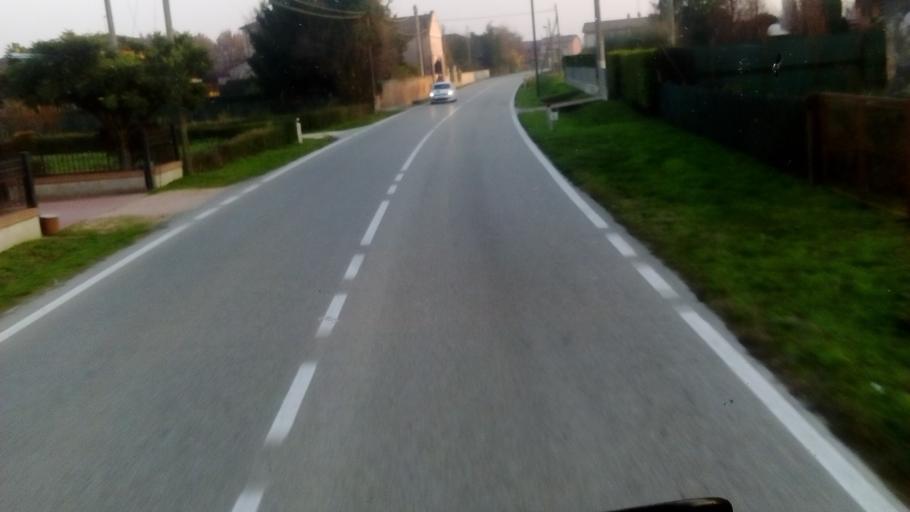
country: IT
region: Veneto
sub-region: Provincia di Padova
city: Tribano
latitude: 45.2218
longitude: 11.8299
